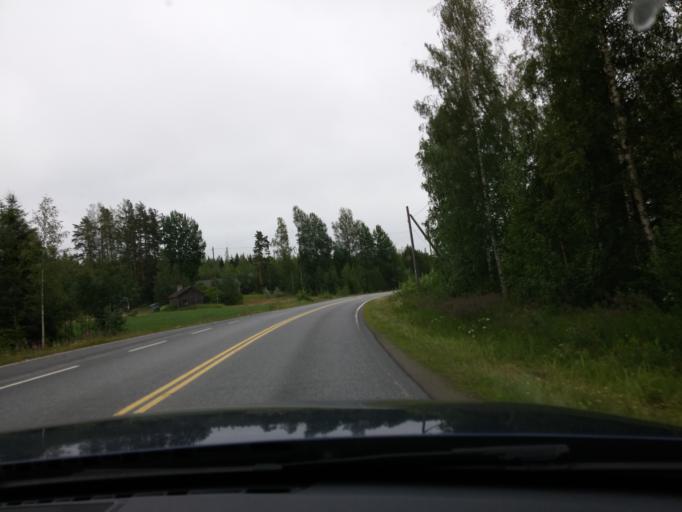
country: FI
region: Central Finland
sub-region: Joutsa
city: Joutsa
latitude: 61.7992
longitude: 25.9979
